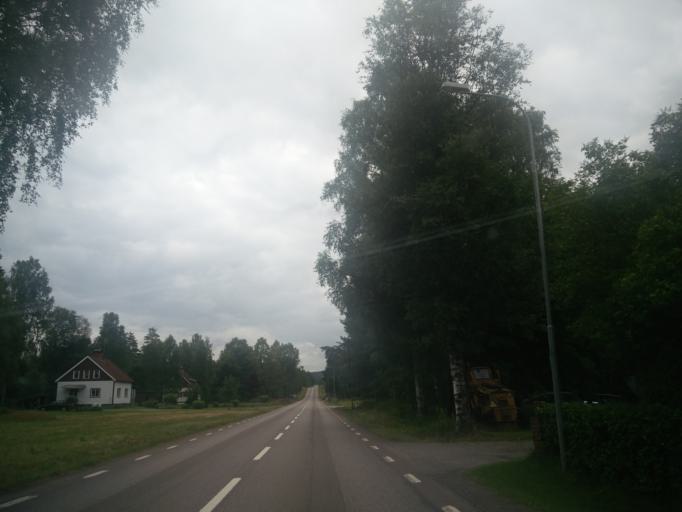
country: SE
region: Vaermland
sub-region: Torsby Kommun
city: Torsby
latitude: 59.9426
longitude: 12.9027
